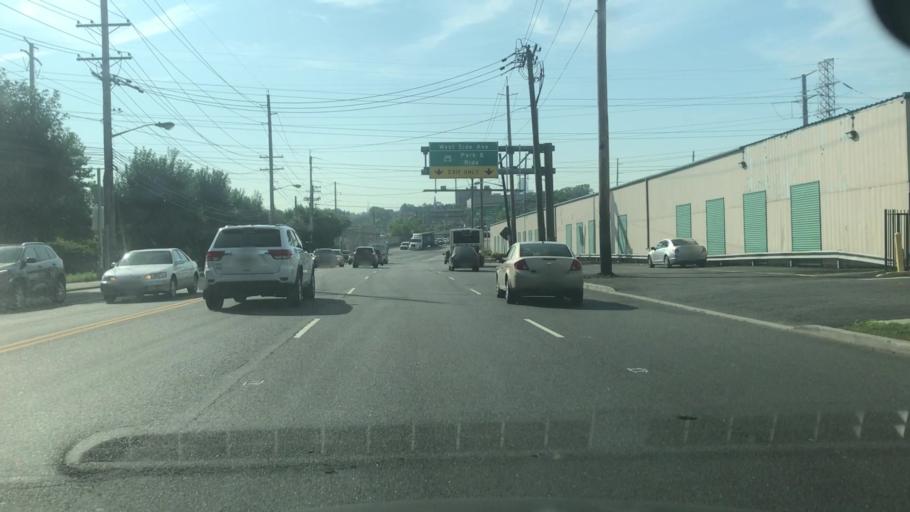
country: US
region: New Jersey
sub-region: Hudson County
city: Secaucus
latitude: 40.7818
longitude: -74.0430
